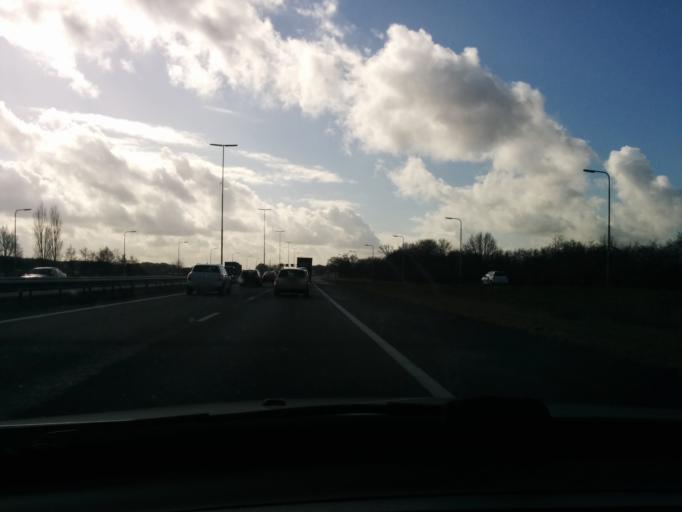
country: NL
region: Utrecht
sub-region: Gemeente De Bilt
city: De Bilt
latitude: 52.1397
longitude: 5.1569
